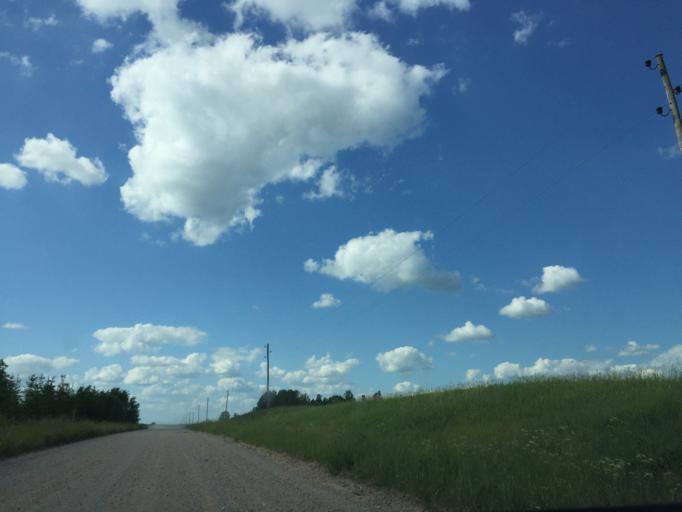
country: LV
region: Jaunpils
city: Jaunpils
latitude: 56.8186
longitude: 23.0685
